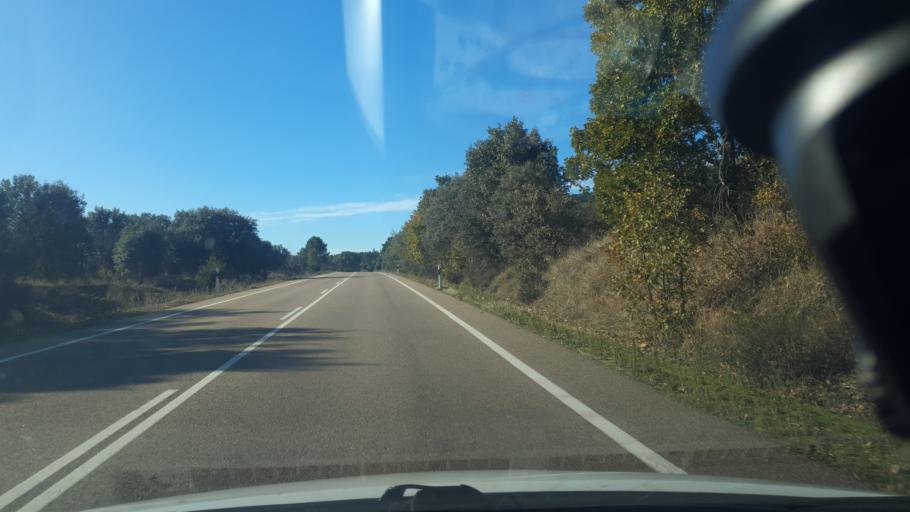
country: ES
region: Castille and Leon
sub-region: Provincia de Avila
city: Arenas de San Pedro
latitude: 40.1727
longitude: -5.0951
